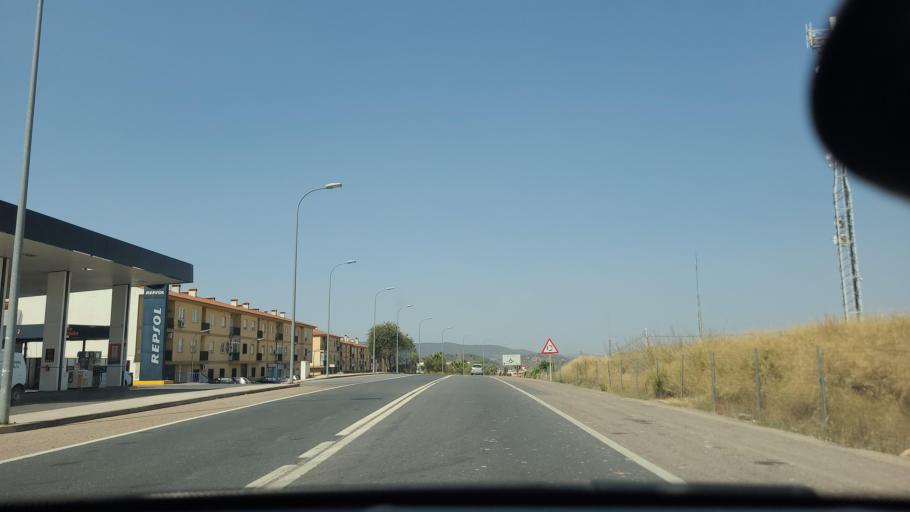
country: ES
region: Extremadura
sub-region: Provincia de Badajoz
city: Zafra
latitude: 38.4306
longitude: -6.4169
